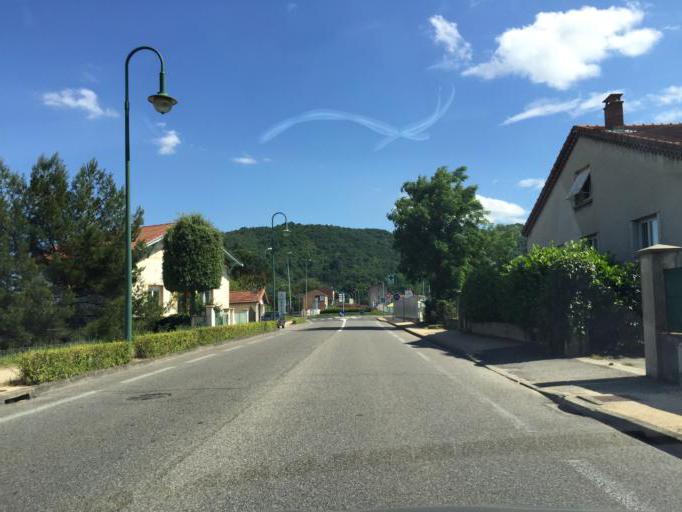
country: FR
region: Rhone-Alpes
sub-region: Departement de l'Ardeche
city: Saint-Jean-de-Muzols
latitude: 45.0774
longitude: 4.8151
